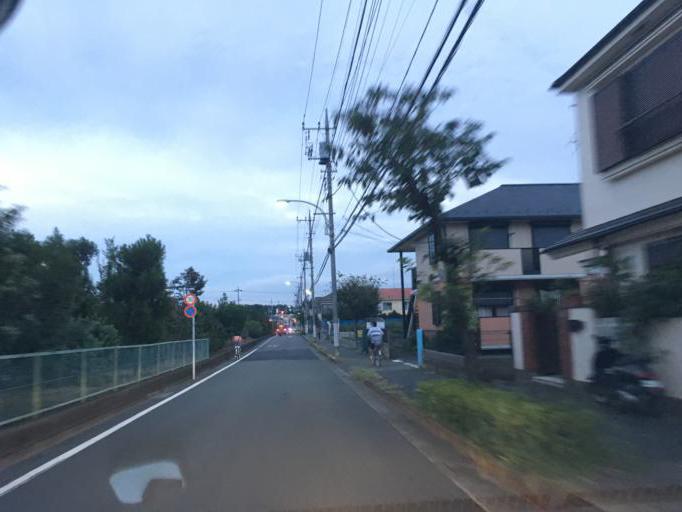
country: JP
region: Tokyo
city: Kokubunji
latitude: 35.7177
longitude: 139.4562
